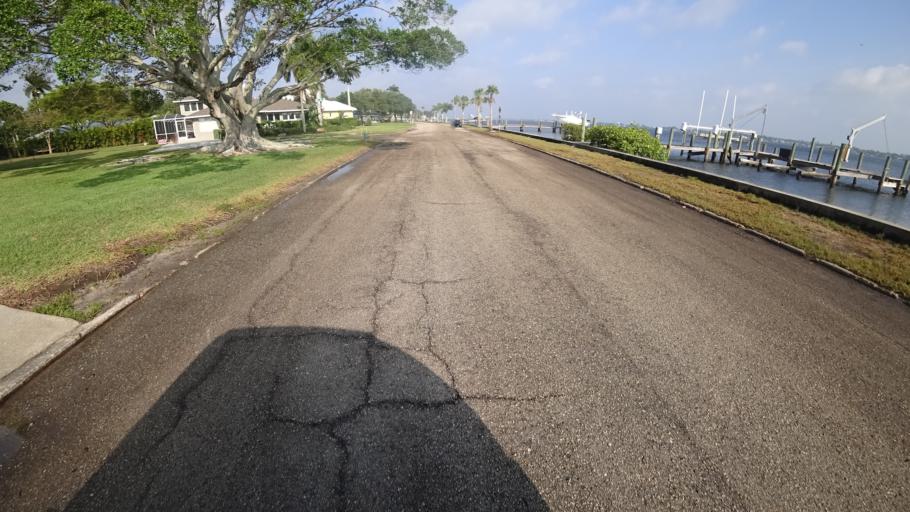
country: US
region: Florida
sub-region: Manatee County
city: Bradenton
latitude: 27.4996
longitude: -82.5840
